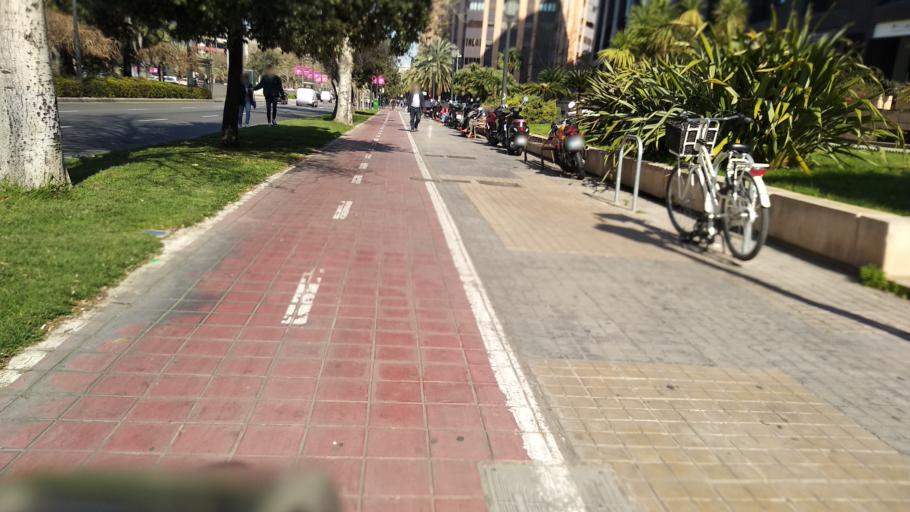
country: ES
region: Valencia
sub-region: Provincia de Valencia
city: Valencia
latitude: 39.4713
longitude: -0.3569
